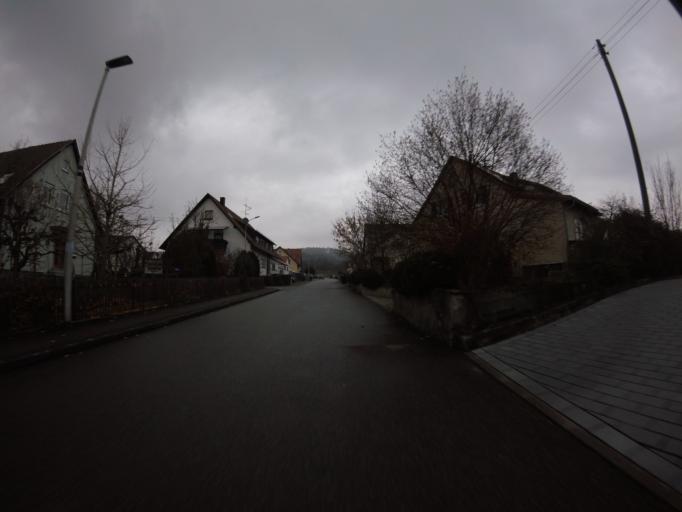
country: DE
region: Baden-Wuerttemberg
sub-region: Regierungsbezirk Stuttgart
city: Aspach
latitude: 48.9910
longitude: 9.4103
